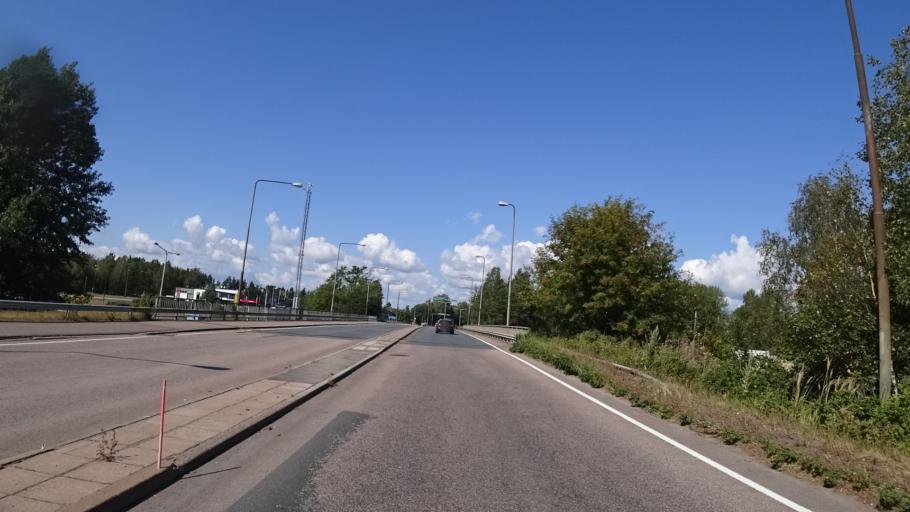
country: FI
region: Kymenlaakso
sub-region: Kotka-Hamina
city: Karhula
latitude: 60.5216
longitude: 26.9494
